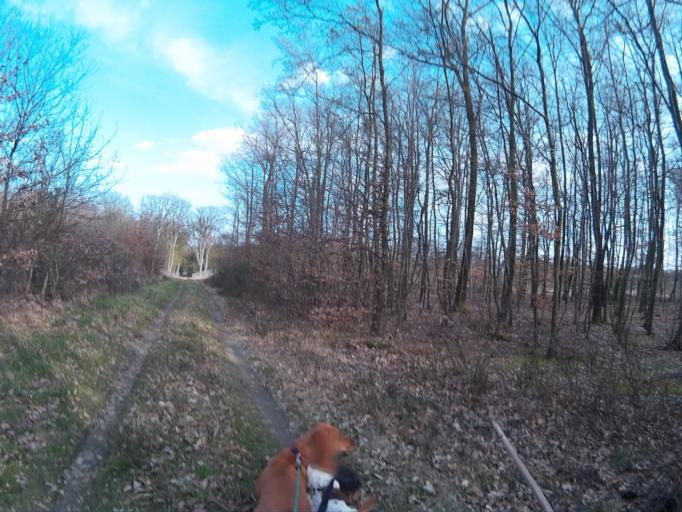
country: HU
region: Vas
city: Sarvar
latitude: 47.1945
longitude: 16.9944
